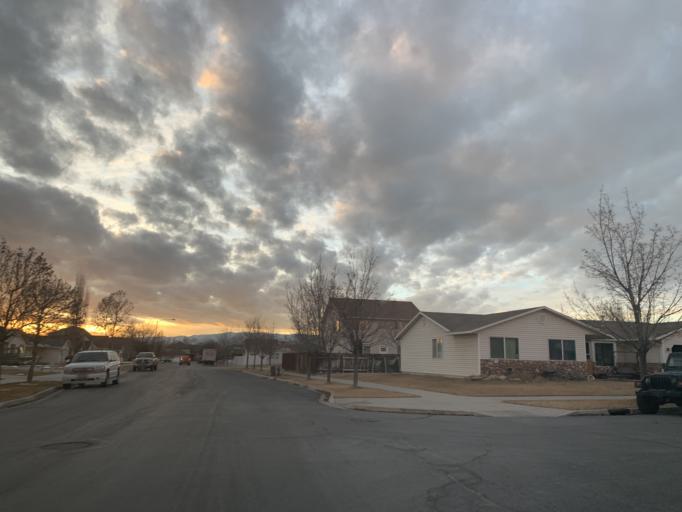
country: US
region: Utah
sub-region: Utah County
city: Provo
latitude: 40.2394
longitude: -111.7032
